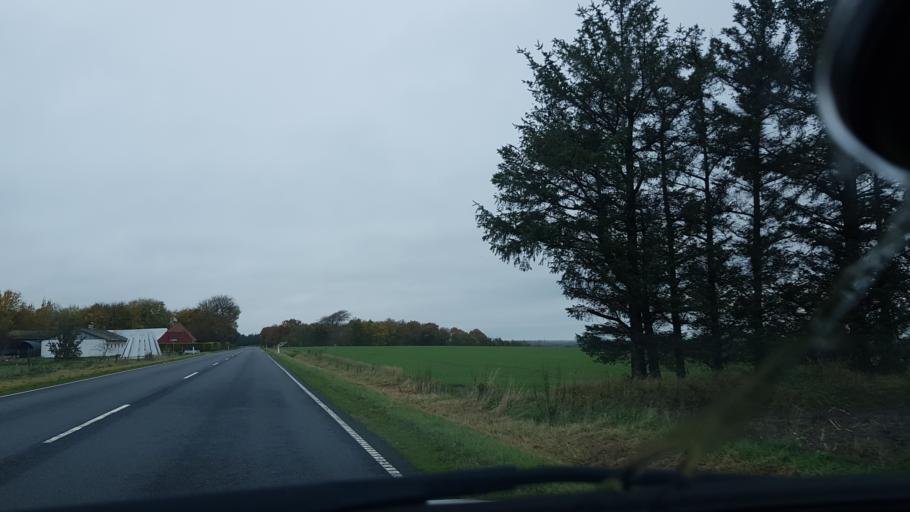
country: DK
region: South Denmark
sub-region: Esbjerg Kommune
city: Ribe
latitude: 55.2758
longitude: 8.8638
